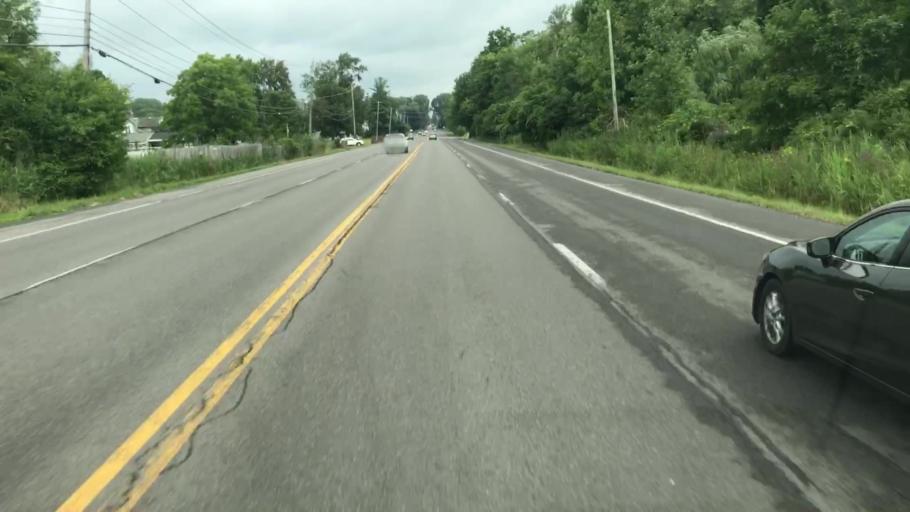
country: US
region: New York
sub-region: Onondaga County
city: Liverpool
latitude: 43.1450
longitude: -76.2071
